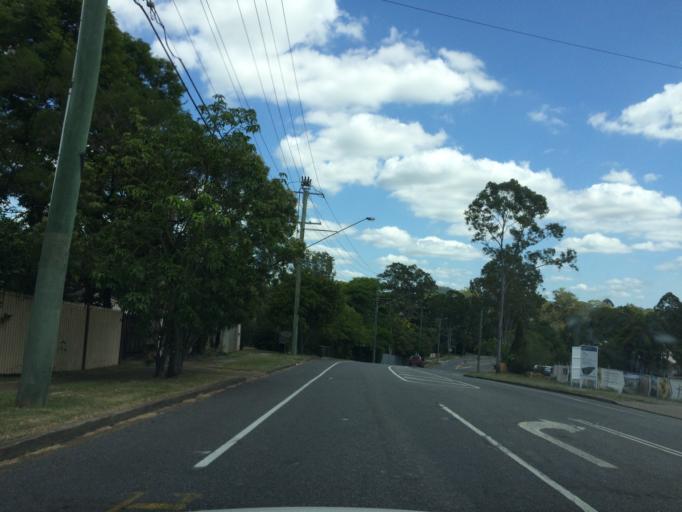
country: AU
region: Queensland
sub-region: Brisbane
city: Kenmore Hills
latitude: -27.5066
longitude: 152.9362
